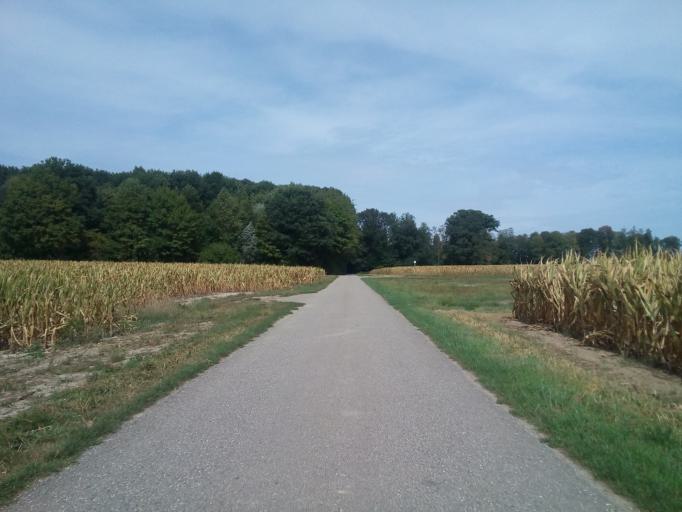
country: DE
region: Baden-Wuerttemberg
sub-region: Karlsruhe Region
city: Zell
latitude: 48.7058
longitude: 8.0459
